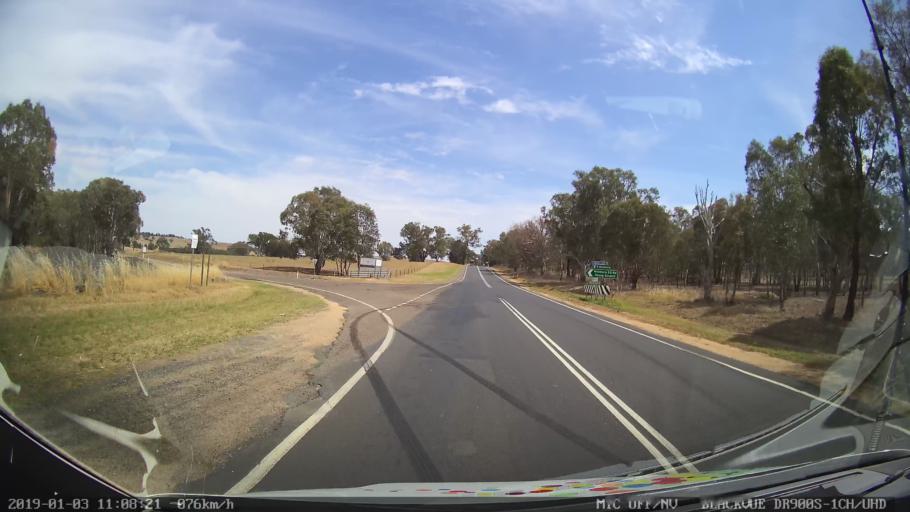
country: AU
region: New South Wales
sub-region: Young
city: Young
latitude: -34.2503
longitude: 148.2575
